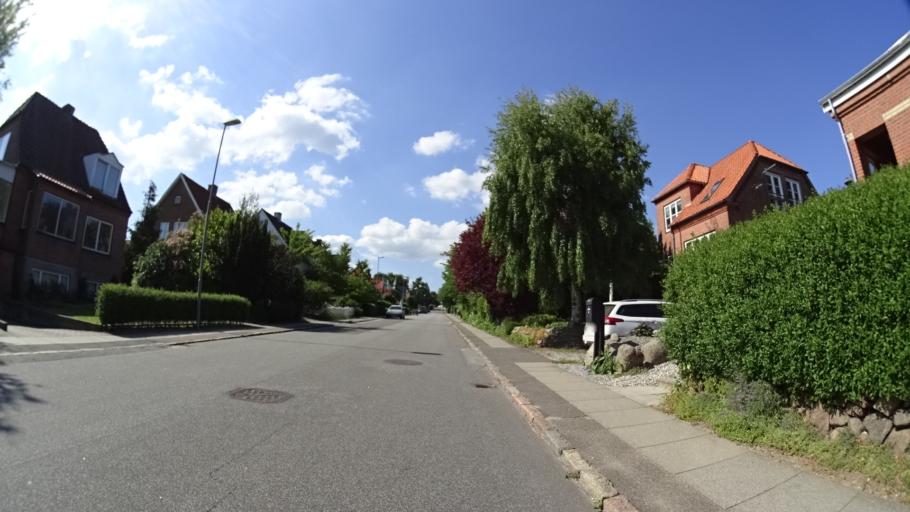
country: DK
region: Central Jutland
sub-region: Arhus Kommune
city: Stavtrup
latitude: 56.1524
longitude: 10.1541
